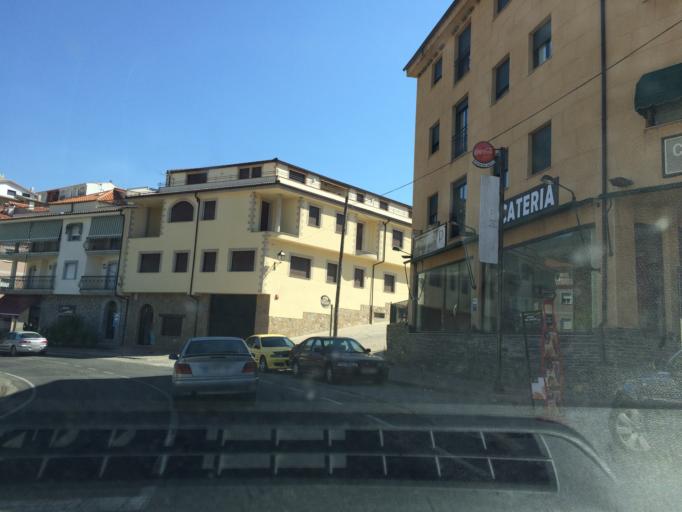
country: ES
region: Extremadura
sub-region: Provincia de Caceres
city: Cabezuela del Valle
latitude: 40.1901
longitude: -5.8063
